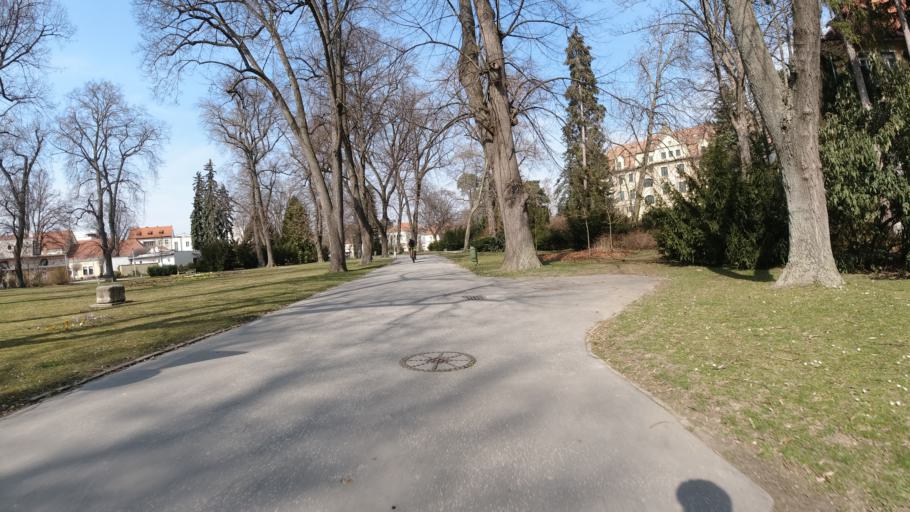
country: SK
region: Trnavsky
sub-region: Okres Trnava
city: Piestany
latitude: 48.5892
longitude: 17.8383
